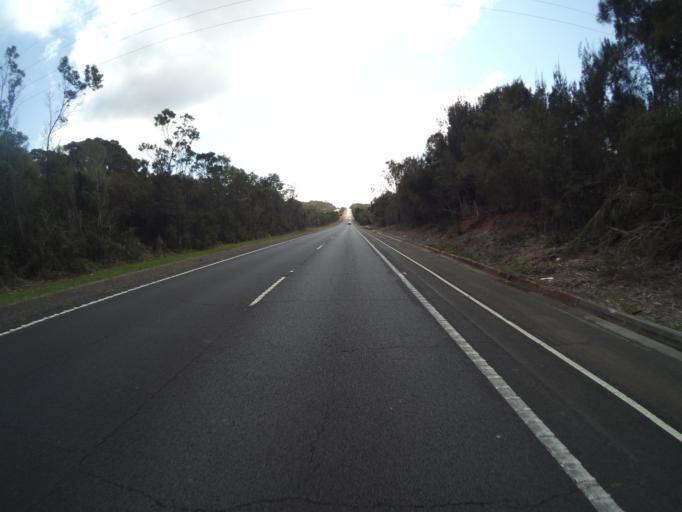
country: AU
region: New South Wales
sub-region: Wollongong
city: Helensburgh
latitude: -34.2189
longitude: 150.9548
